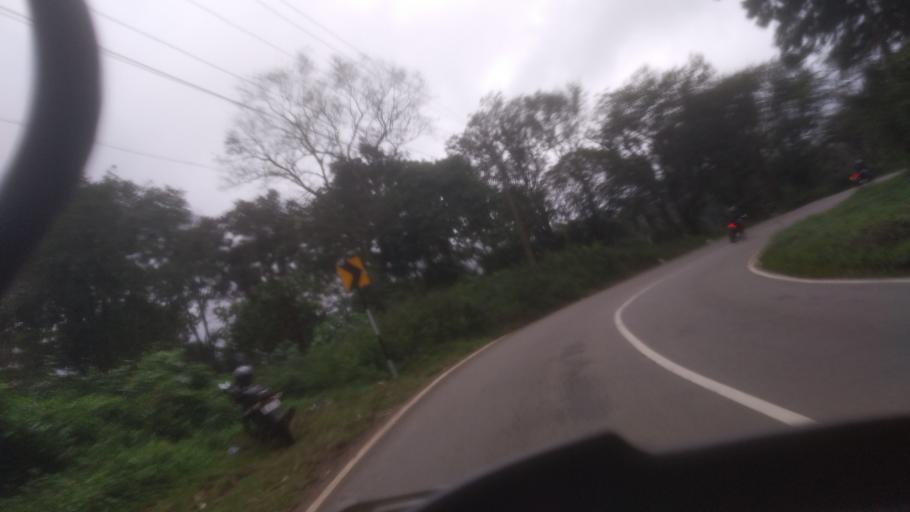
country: IN
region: Tamil Nadu
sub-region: Theni
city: Kombai
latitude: 9.8921
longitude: 77.2040
